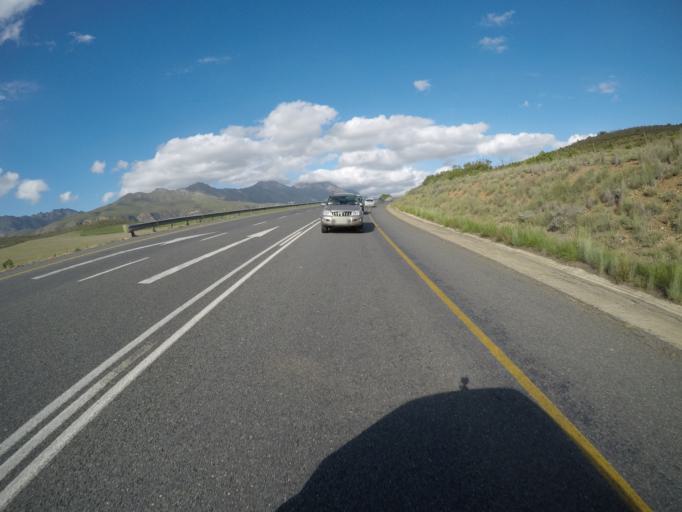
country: ZA
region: Western Cape
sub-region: Cape Winelands District Municipality
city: Ashton
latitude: -33.9498
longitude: 20.2245
